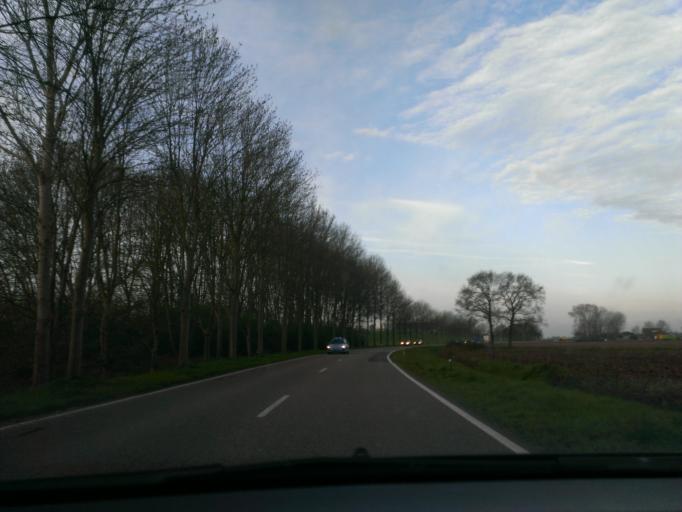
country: NL
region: Gelderland
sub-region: Gemeente Voorst
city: Twello
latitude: 52.2180
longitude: 6.1219
